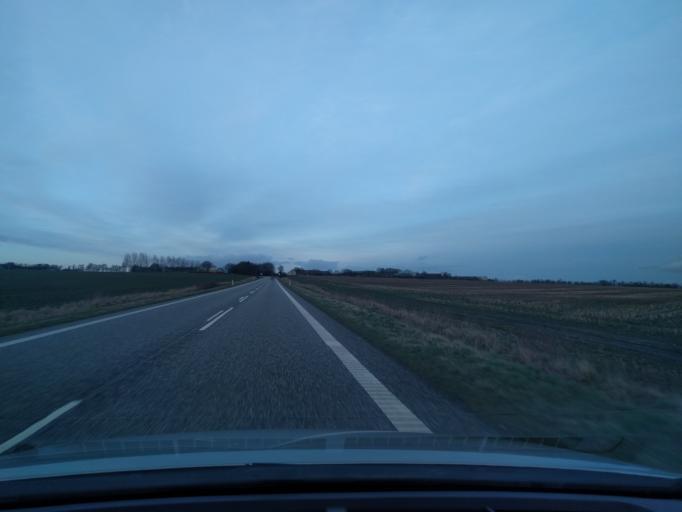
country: DK
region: South Denmark
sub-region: Tonder Kommune
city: Logumkloster
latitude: 55.1287
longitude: 8.9927
